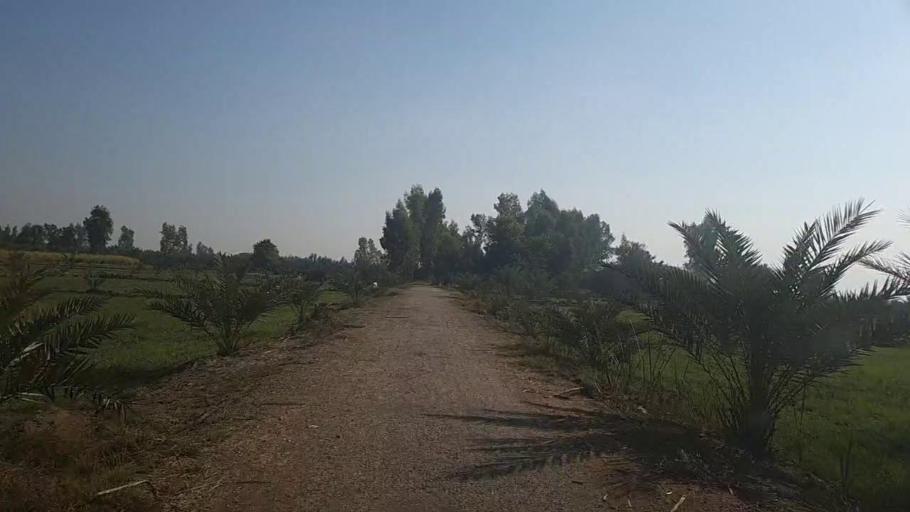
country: PK
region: Sindh
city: Kot Diji
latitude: 27.4333
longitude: 68.7335
